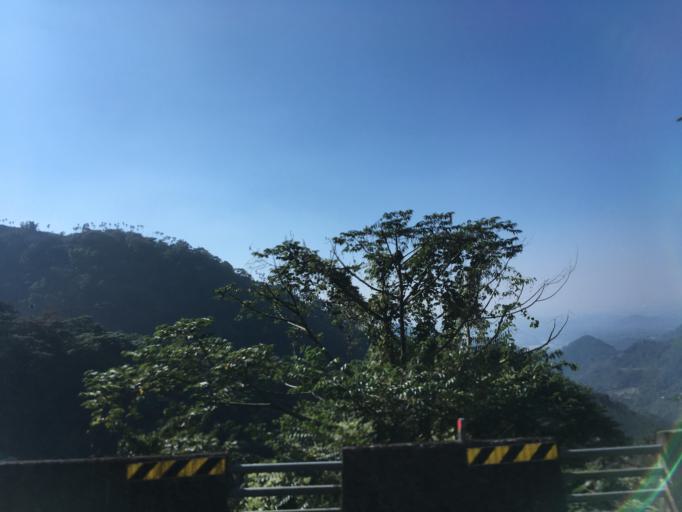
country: TW
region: Taiwan
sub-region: Chiayi
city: Jiayi Shi
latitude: 23.4246
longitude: 120.6430
